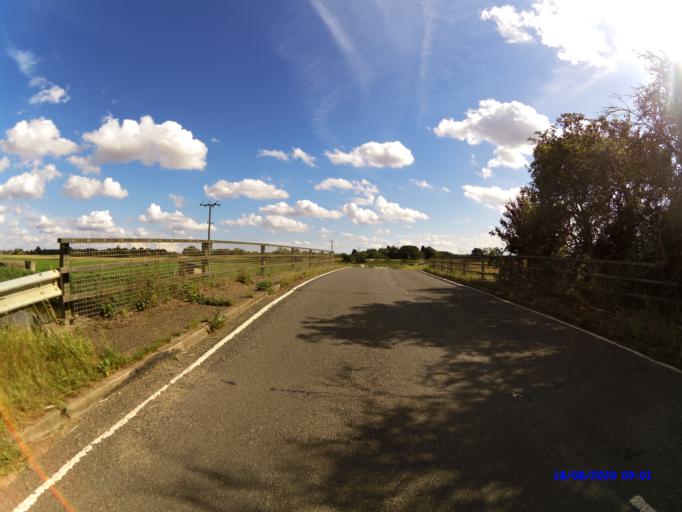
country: GB
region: England
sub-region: Cambridgeshire
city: Ramsey
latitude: 52.4731
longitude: -0.0954
